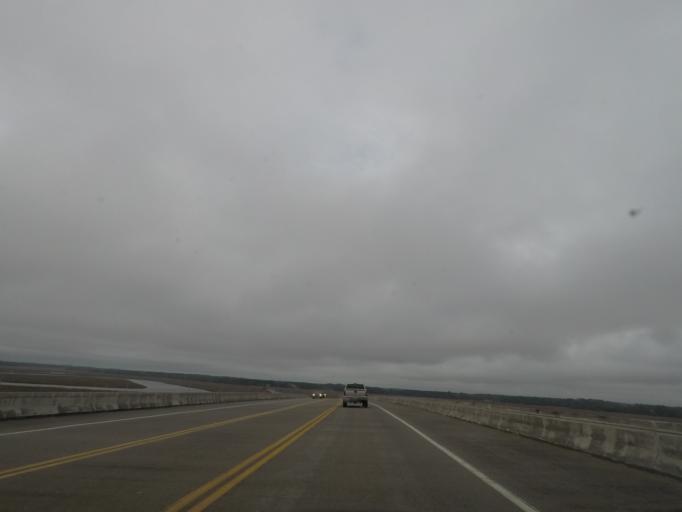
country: US
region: South Carolina
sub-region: Charleston County
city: Meggett
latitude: 32.6376
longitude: -80.3402
